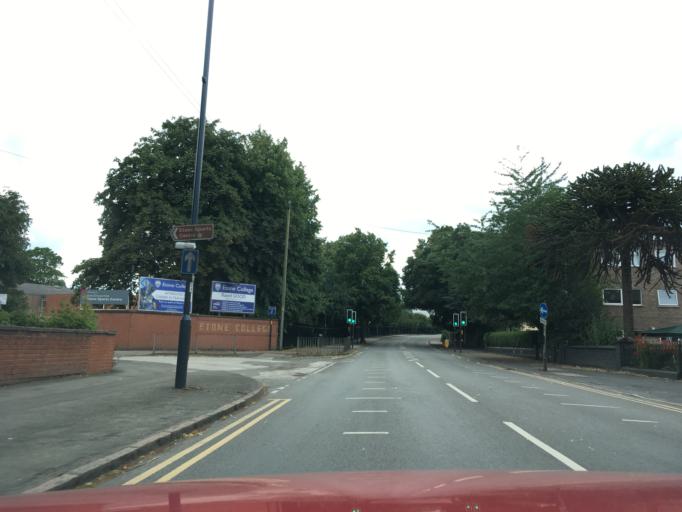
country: GB
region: England
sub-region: Warwickshire
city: Nuneaton
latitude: 52.5267
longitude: -1.4588
